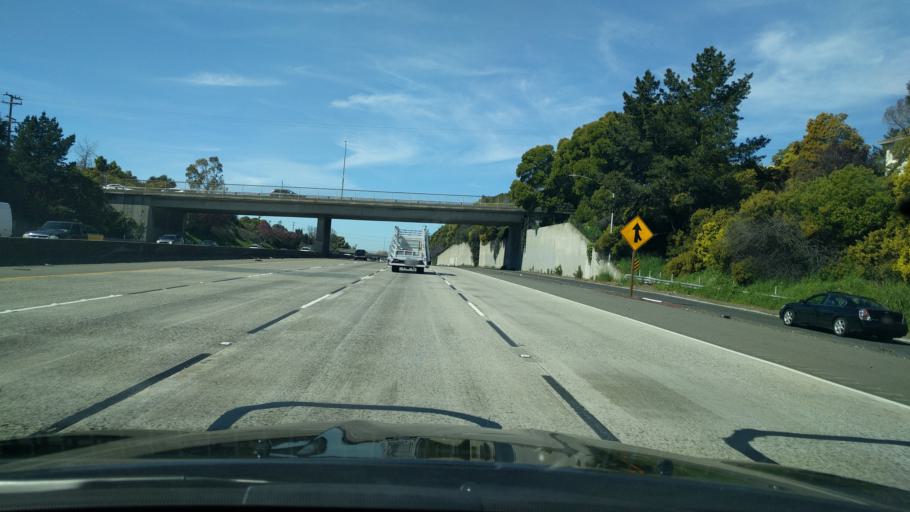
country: US
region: California
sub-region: Alameda County
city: Piedmont
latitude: 37.7991
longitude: -122.2200
